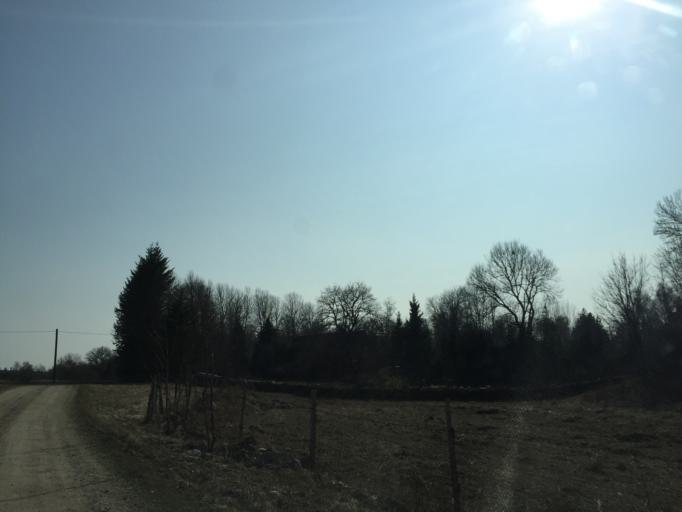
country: EE
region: Saare
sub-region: Orissaare vald
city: Orissaare
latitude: 58.4799
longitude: 23.1220
